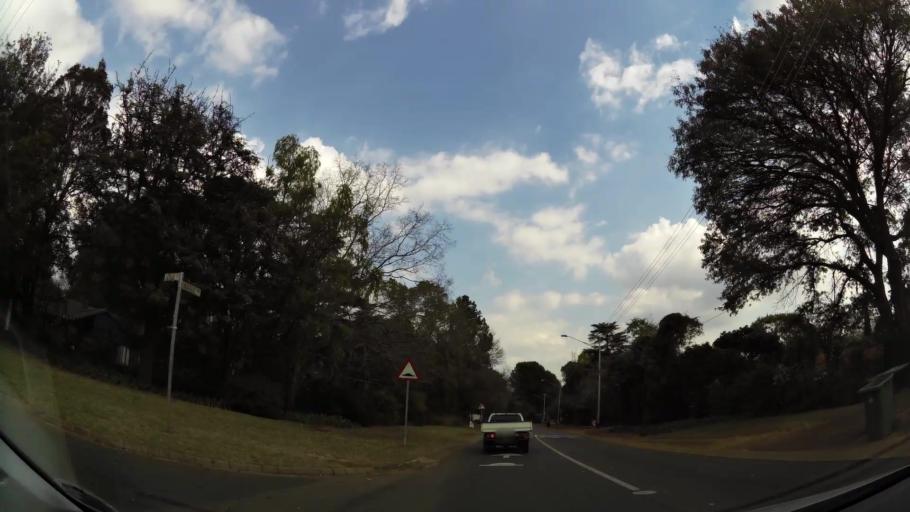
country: ZA
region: Gauteng
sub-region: City of Tshwane Metropolitan Municipality
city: Pretoria
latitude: -25.7500
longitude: 28.3071
